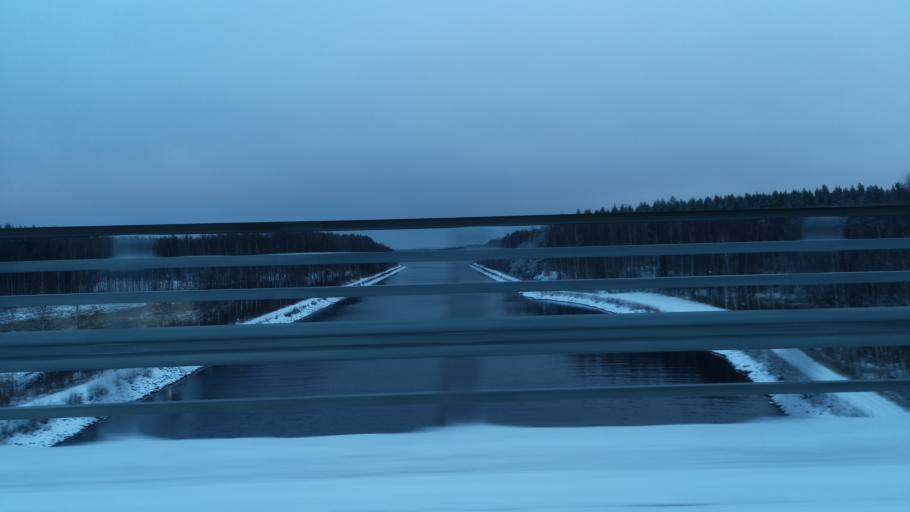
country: FI
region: Southern Savonia
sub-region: Savonlinna
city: Enonkoski
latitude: 62.0982
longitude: 28.6619
